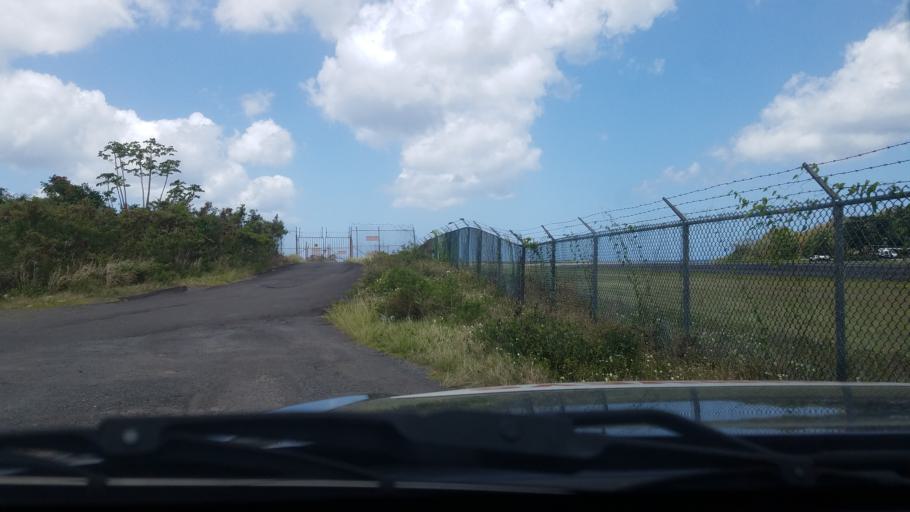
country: LC
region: Castries Quarter
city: Castries
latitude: 14.0180
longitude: -60.9987
